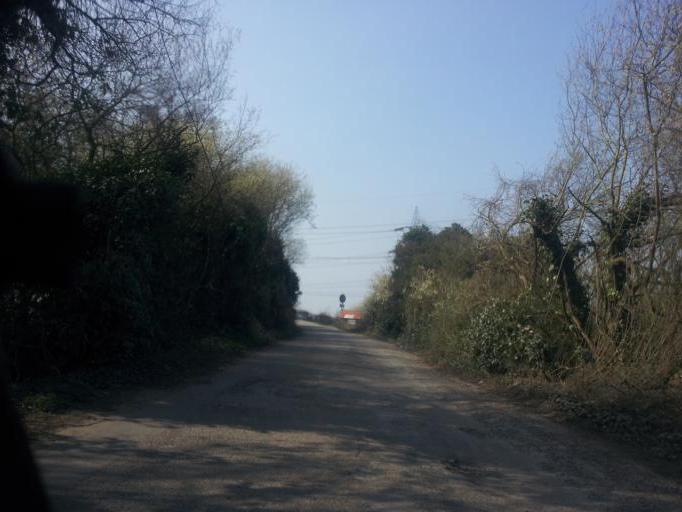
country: GB
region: England
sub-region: Kent
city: Cliffe
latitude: 51.4388
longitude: 0.4512
